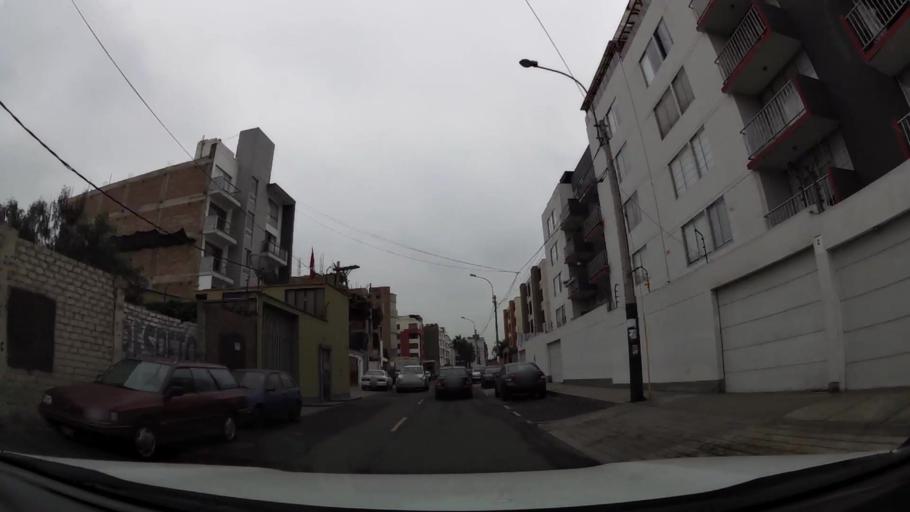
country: PE
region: Lima
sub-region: Lima
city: Surco
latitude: -12.1354
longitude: -77.0065
